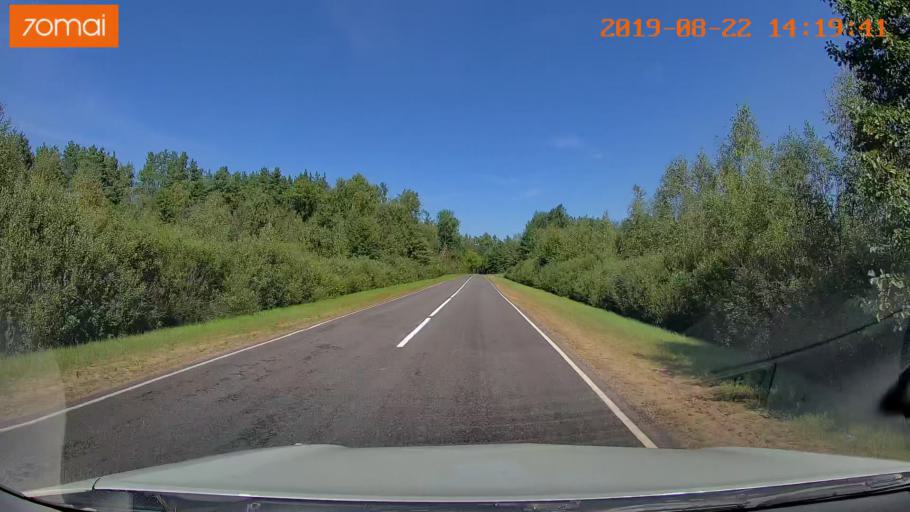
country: BY
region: Mogilev
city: Asipovichy
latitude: 53.2620
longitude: 28.5086
